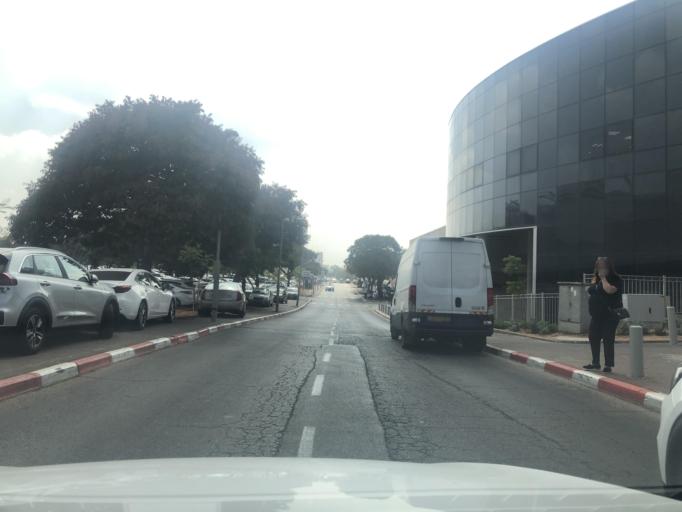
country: IL
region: Tel Aviv
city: Or Yehuda
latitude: 32.0462
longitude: 34.8459
